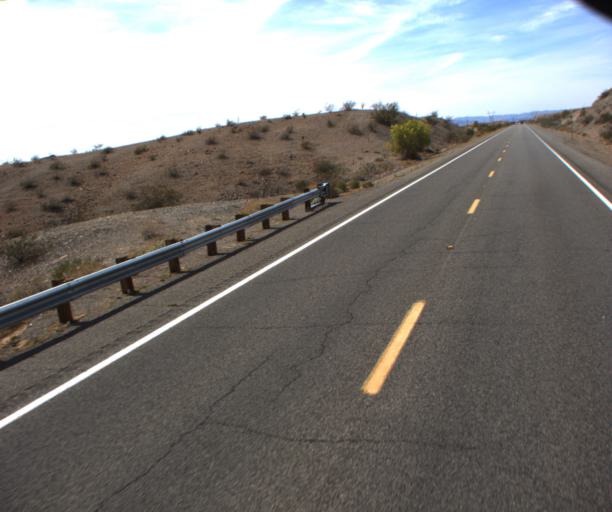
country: US
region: Arizona
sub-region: Mohave County
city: Lake Havasu City
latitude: 34.4411
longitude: -114.2304
